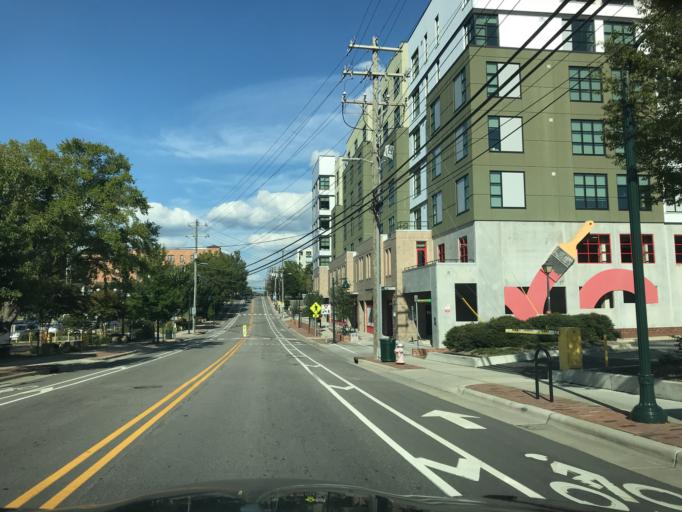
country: US
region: North Carolina
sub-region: Orange County
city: Chapel Hill
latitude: 35.9117
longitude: -79.0623
